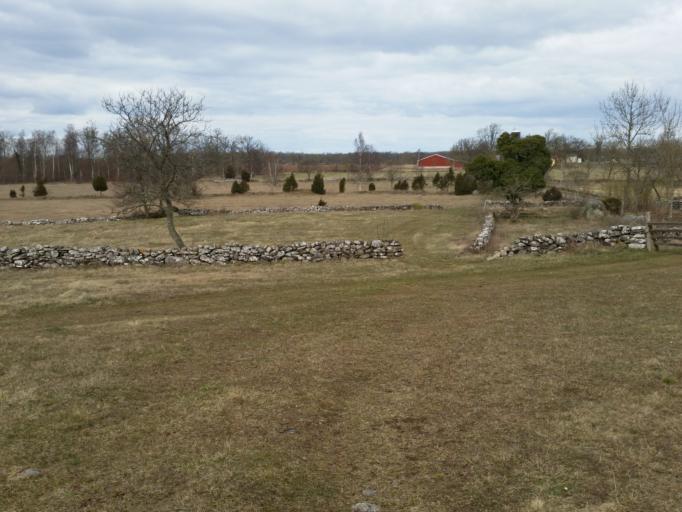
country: SE
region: Kalmar
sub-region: Morbylanga Kommun
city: Sodra Sandby
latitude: 56.6787
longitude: 16.5806
